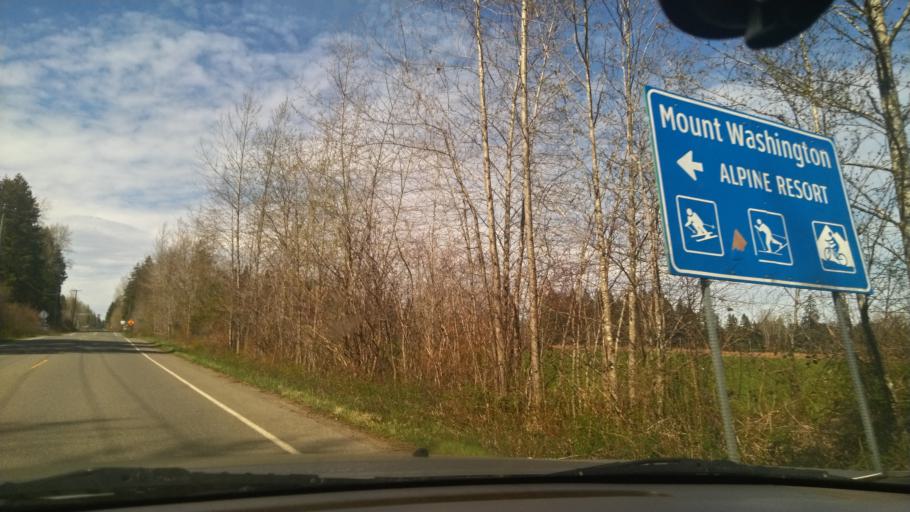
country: CA
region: British Columbia
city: Courtenay
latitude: 49.7043
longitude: -125.0226
